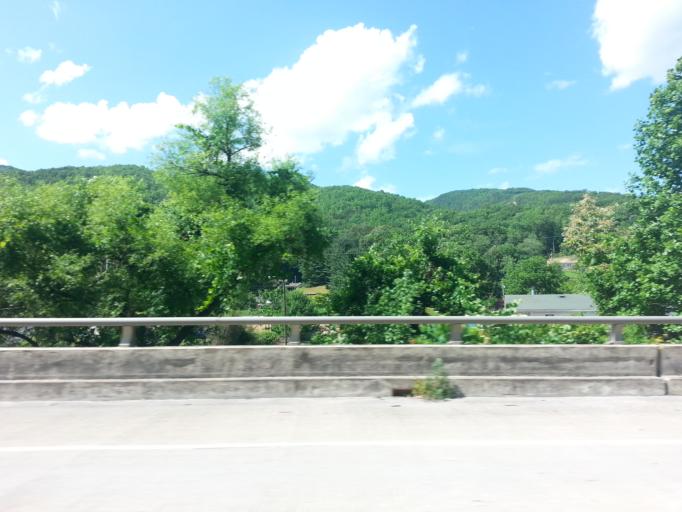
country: US
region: Kentucky
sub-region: Harlan County
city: Harlan
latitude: 36.9249
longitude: -83.1683
